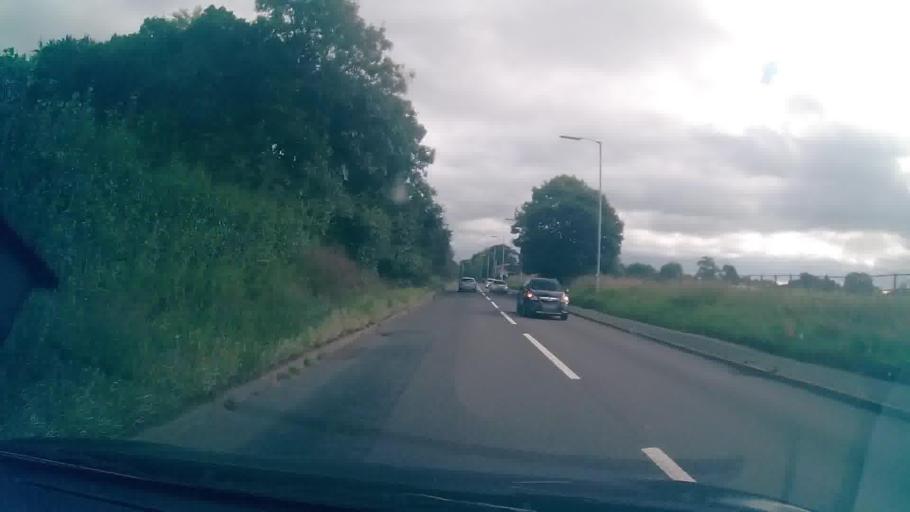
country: GB
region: England
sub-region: Shropshire
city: Whitchurch
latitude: 52.9807
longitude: -2.7085
